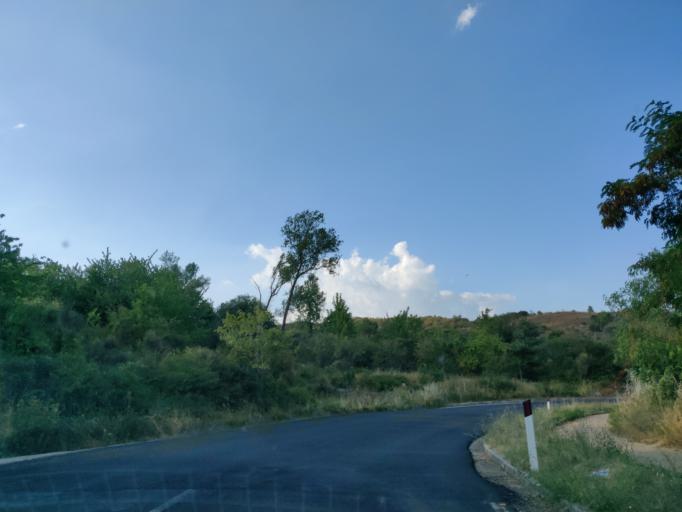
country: IT
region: Tuscany
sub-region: Provincia di Siena
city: Abbadia San Salvatore
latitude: 42.8658
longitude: 11.6795
